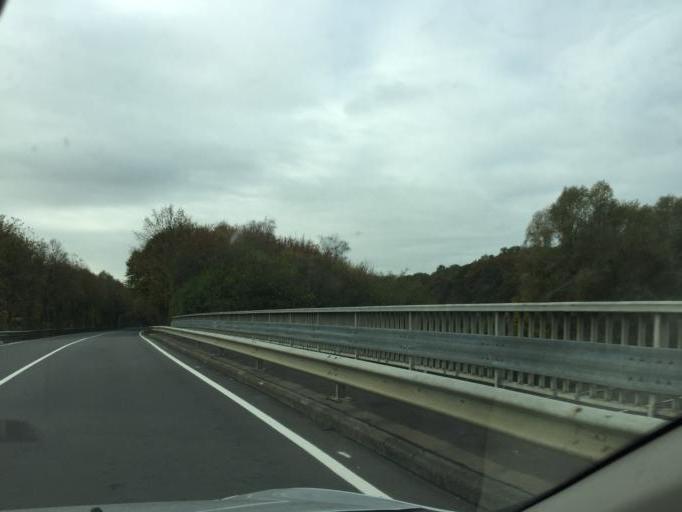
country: LU
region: Luxembourg
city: Capellen
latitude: 49.6350
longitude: 5.9807
